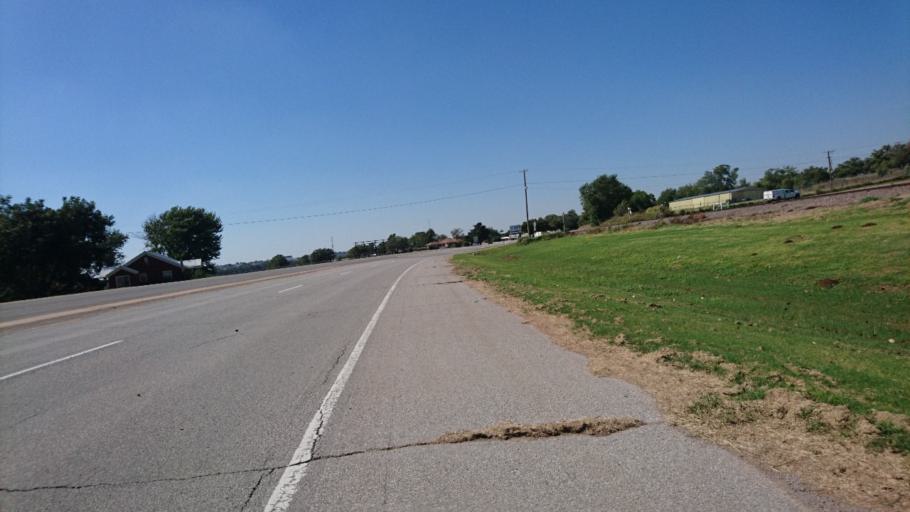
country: US
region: Oklahoma
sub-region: Custer County
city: Clinton
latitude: 35.5142
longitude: -98.9396
